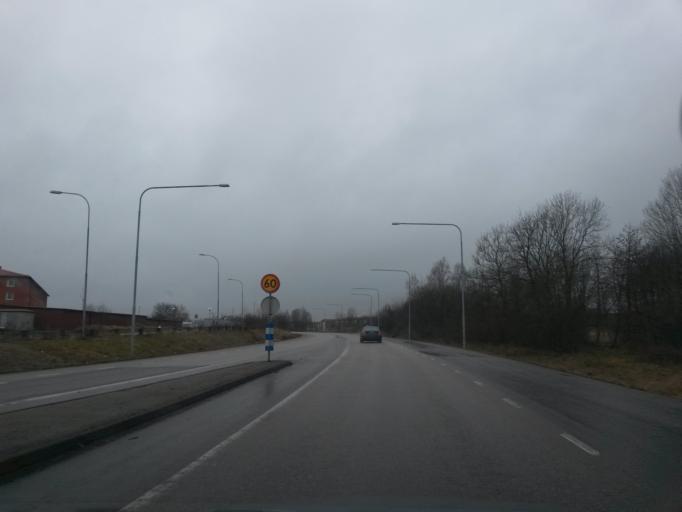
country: SE
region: Vaestra Goetaland
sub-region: Vanersborgs Kommun
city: Vanersborg
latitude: 58.3648
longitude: 12.3478
